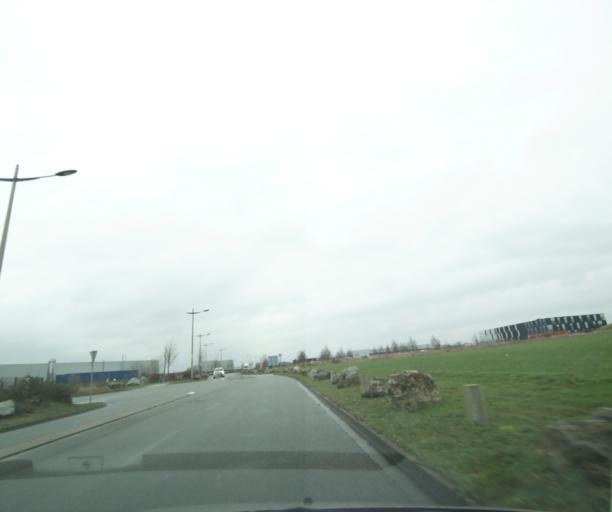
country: FR
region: Nord-Pas-de-Calais
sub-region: Departement du Nord
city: Haulchin
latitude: 50.3317
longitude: 3.4380
